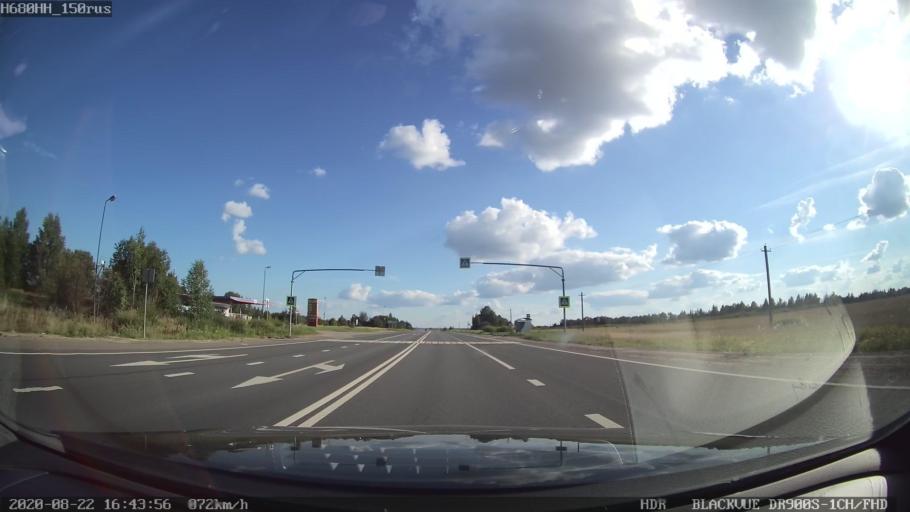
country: RU
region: Tverskaya
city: Rameshki
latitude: 57.3150
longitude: 36.0885
